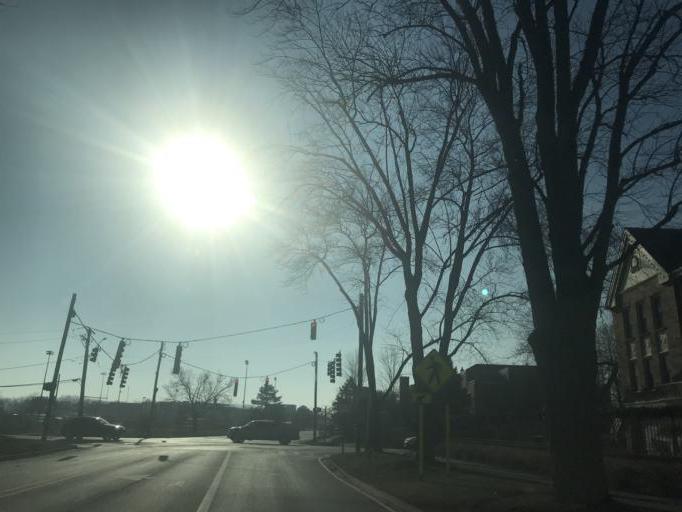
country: US
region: Illinois
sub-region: Cook County
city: Northfield
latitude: 42.0946
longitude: -87.7663
